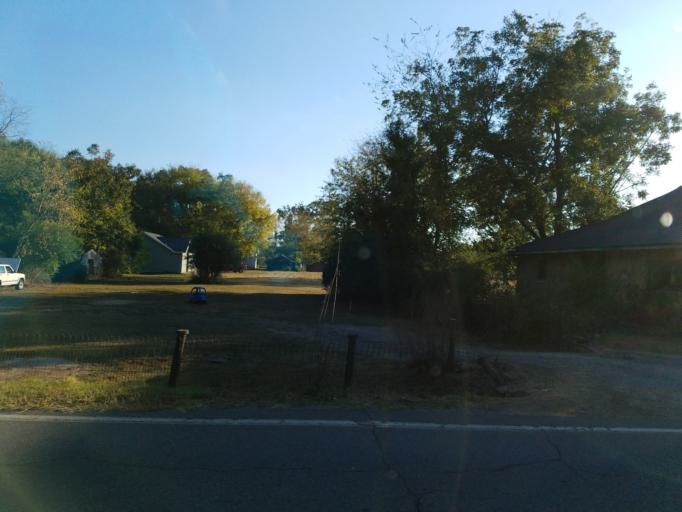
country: US
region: Georgia
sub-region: Bartow County
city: Euharlee
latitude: 34.2387
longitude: -84.9471
